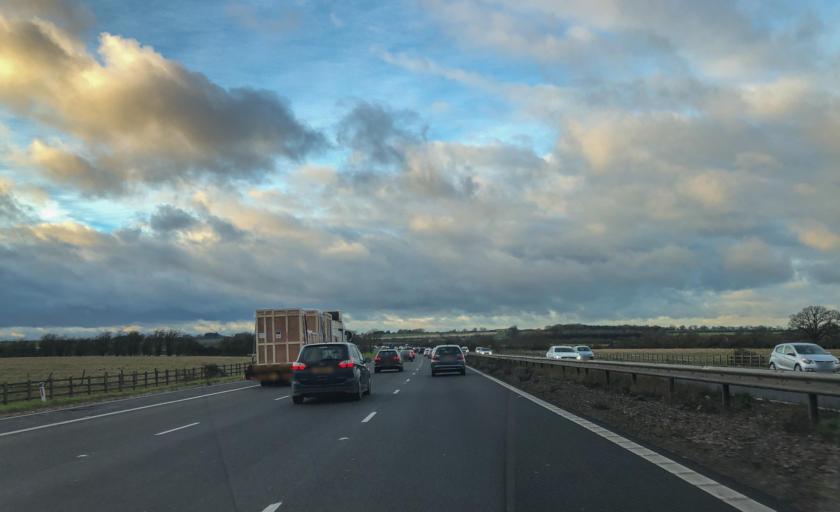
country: GB
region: England
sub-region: Oxfordshire
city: Thame
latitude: 51.7149
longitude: -1.0217
